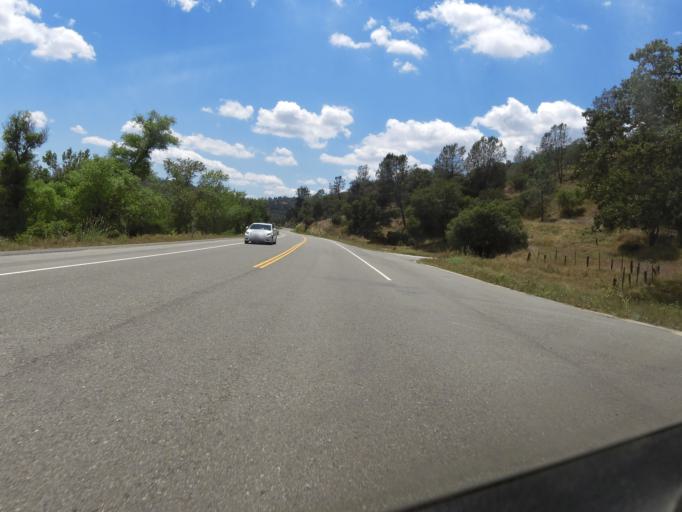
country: US
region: California
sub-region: Madera County
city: Coarsegold
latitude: 37.1669
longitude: -119.6394
